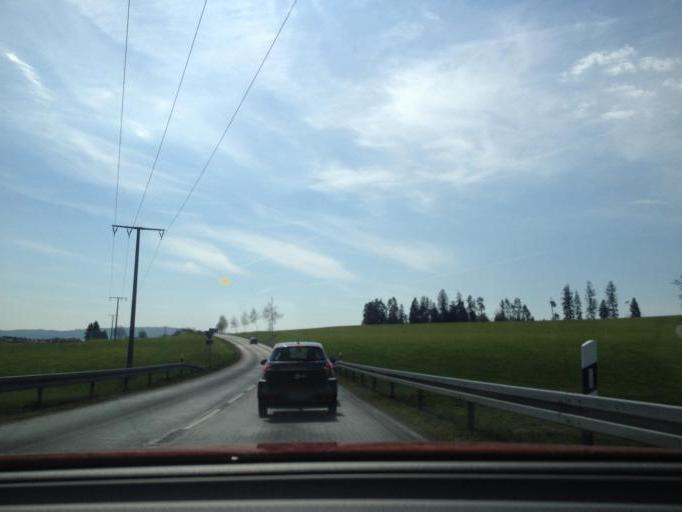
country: DE
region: Bavaria
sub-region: Upper Franconia
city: Munchberg
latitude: 50.1872
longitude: 11.7721
